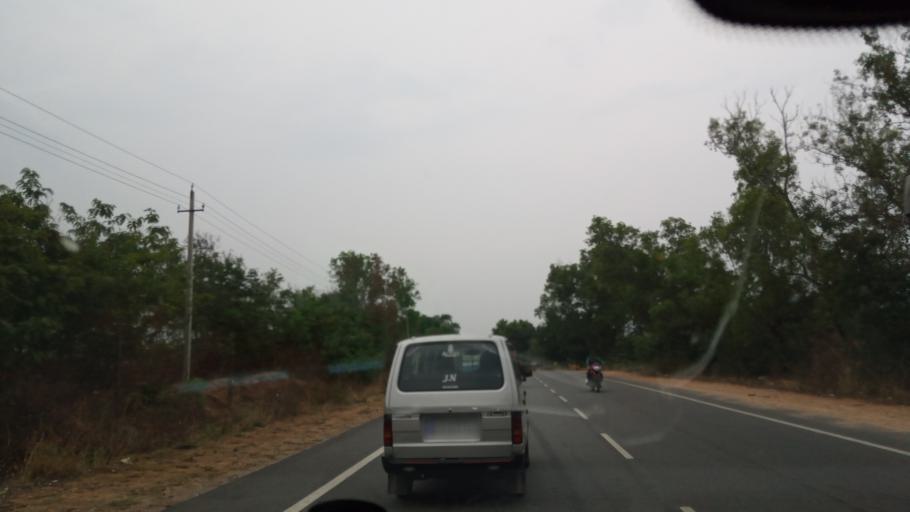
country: IN
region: Karnataka
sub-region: Mandya
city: Belluru
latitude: 12.9414
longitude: 76.7513
